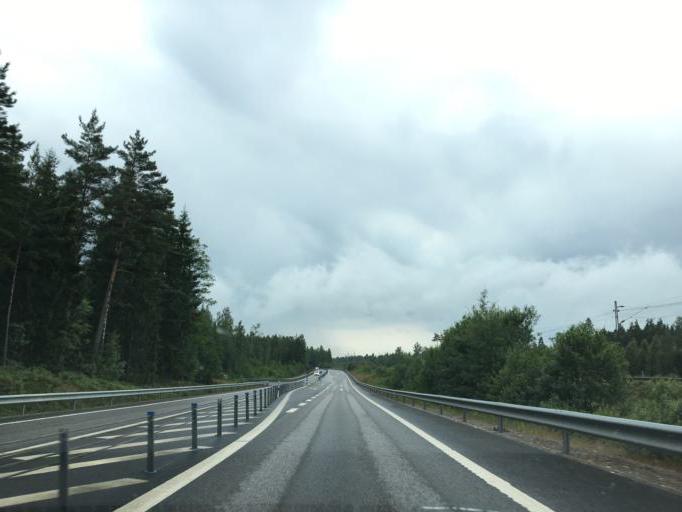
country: SE
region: OEstergoetland
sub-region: Norrkopings Kommun
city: Jursla
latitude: 58.8122
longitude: 16.1534
